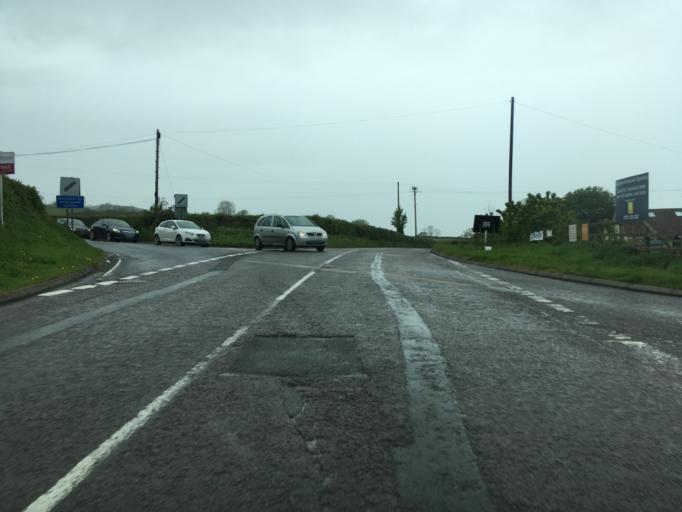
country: GB
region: England
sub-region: Bath and North East Somerset
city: Compton Martin
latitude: 51.3087
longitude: -2.6432
